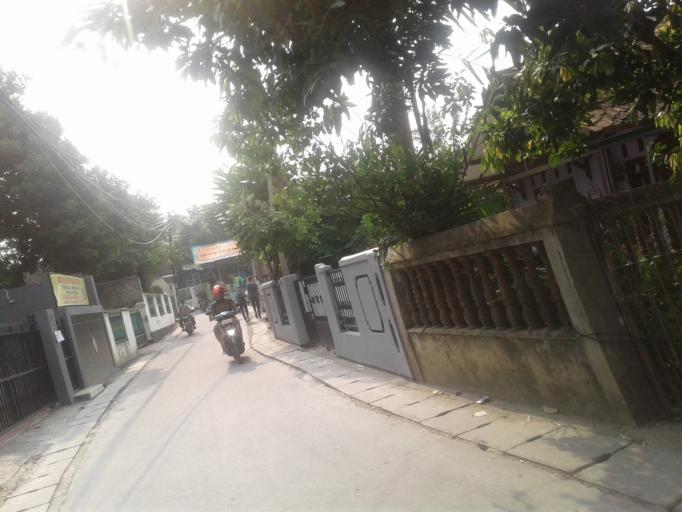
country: ID
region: West Java
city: Depok
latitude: -6.3727
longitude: 106.8373
